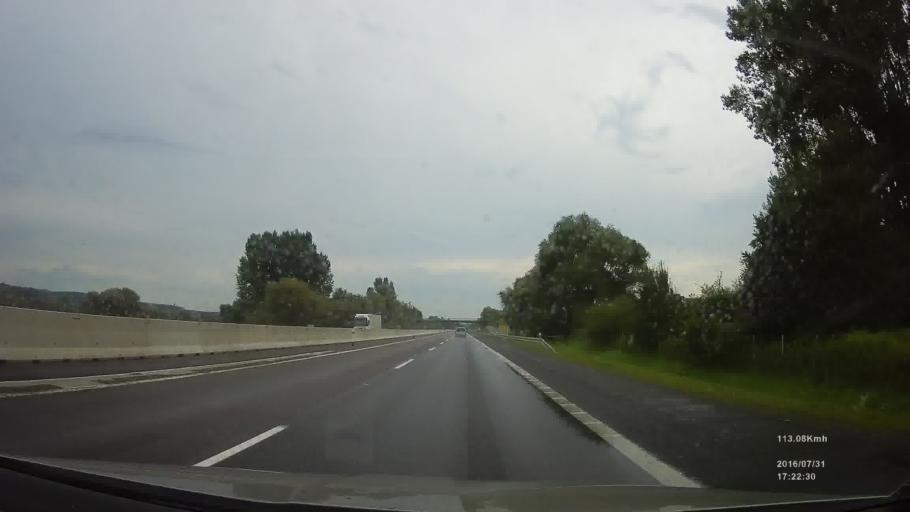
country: SK
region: Kosicky
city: Kosice
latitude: 48.8025
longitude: 21.3100
